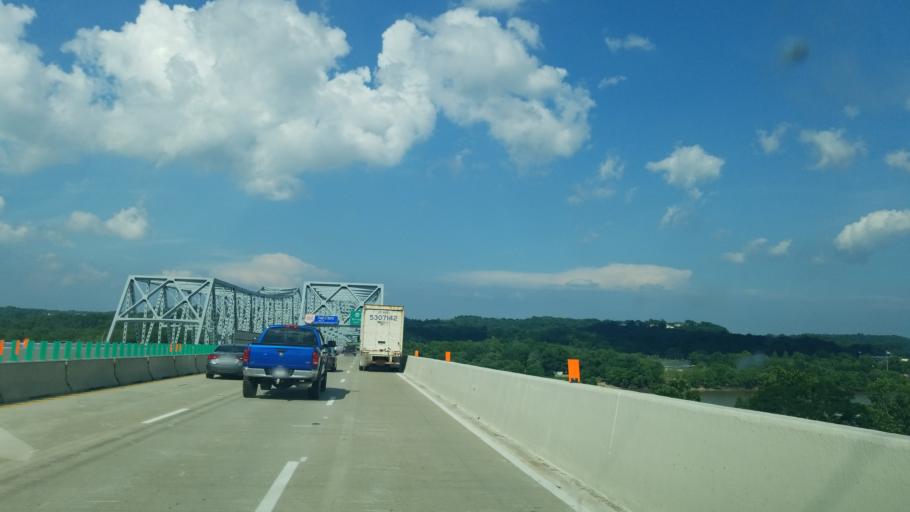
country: US
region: Kentucky
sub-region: Campbell County
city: Fort Thomas
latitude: 39.0553
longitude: -84.4343
